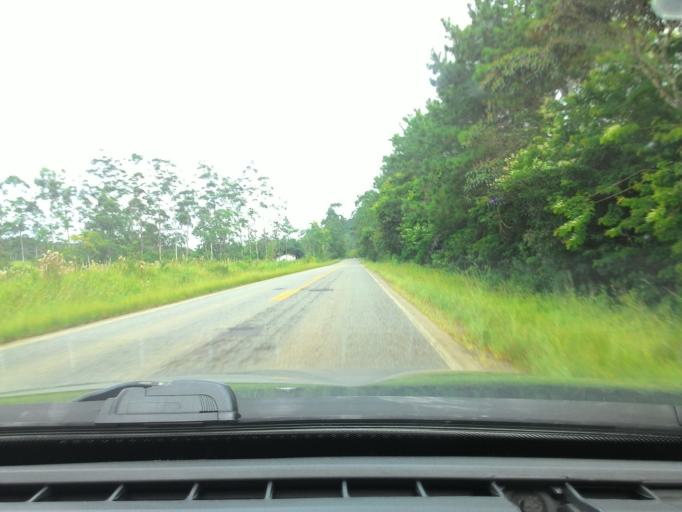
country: BR
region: Sao Paulo
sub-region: Pariquera-Acu
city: Pariquera Acu
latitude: -24.7324
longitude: -47.8281
